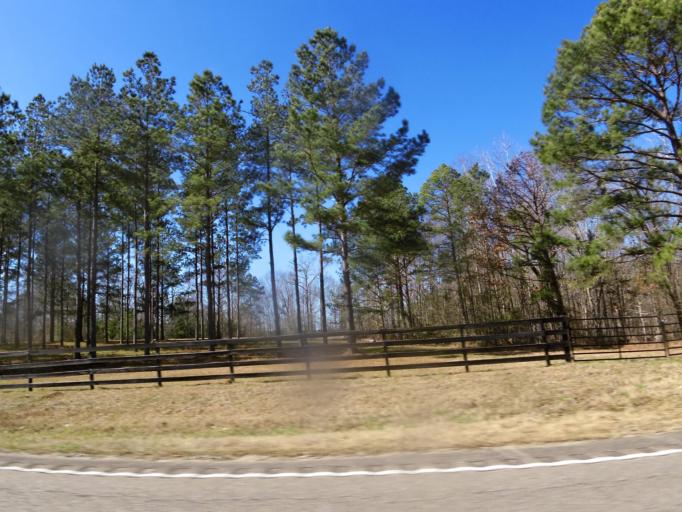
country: US
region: Alabama
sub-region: Bullock County
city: Union Springs
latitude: 32.1322
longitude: -85.7679
